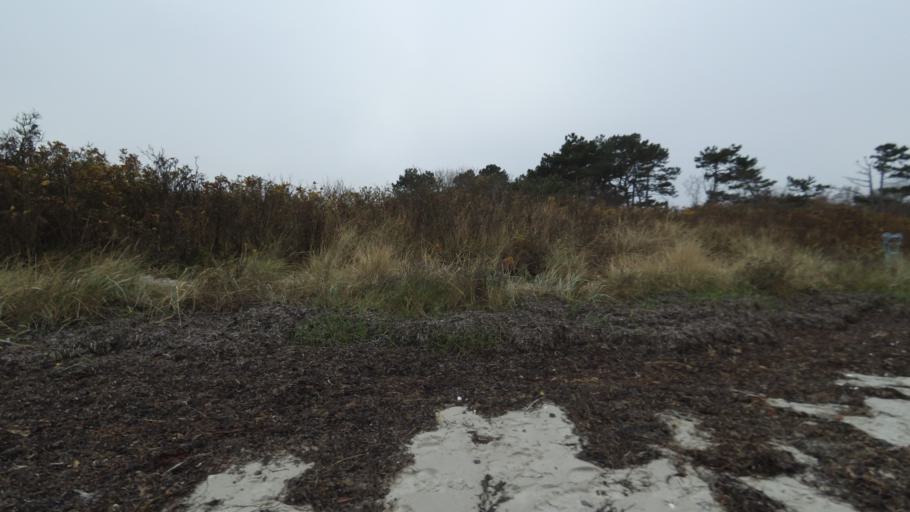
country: DK
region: Central Jutland
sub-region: Arhus Kommune
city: Malling
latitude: 55.9683
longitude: 10.2595
